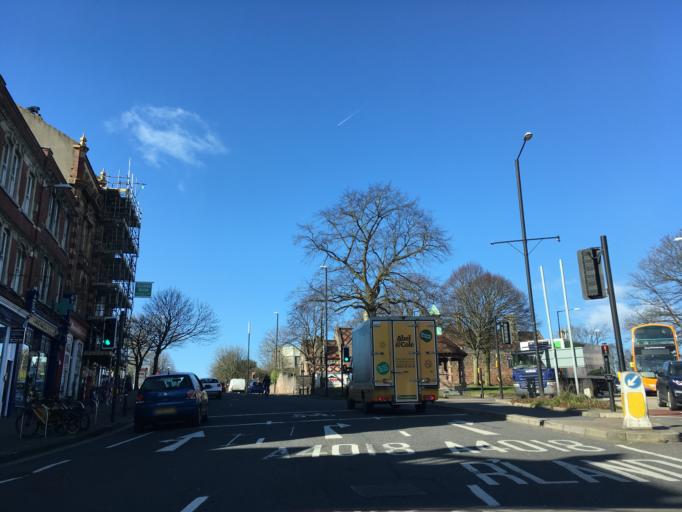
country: GB
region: England
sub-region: Bristol
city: Bristol
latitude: 51.4702
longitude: -2.6150
